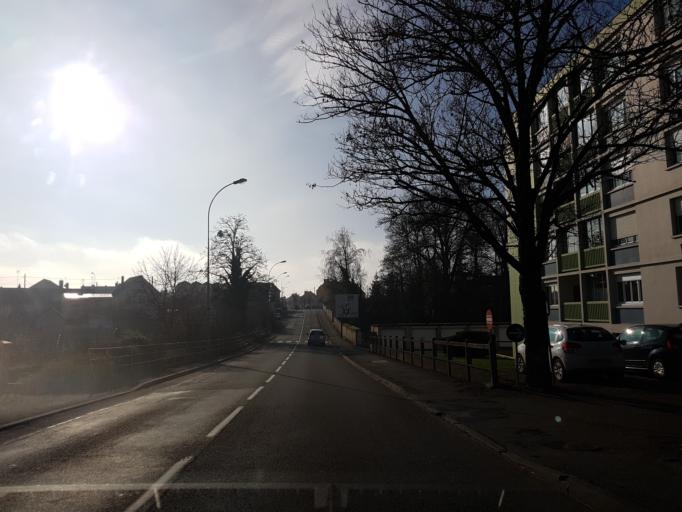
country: FR
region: Bourgogne
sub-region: Departement de Saone-et-Loire
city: Gueugnon
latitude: 46.6027
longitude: 4.0702
